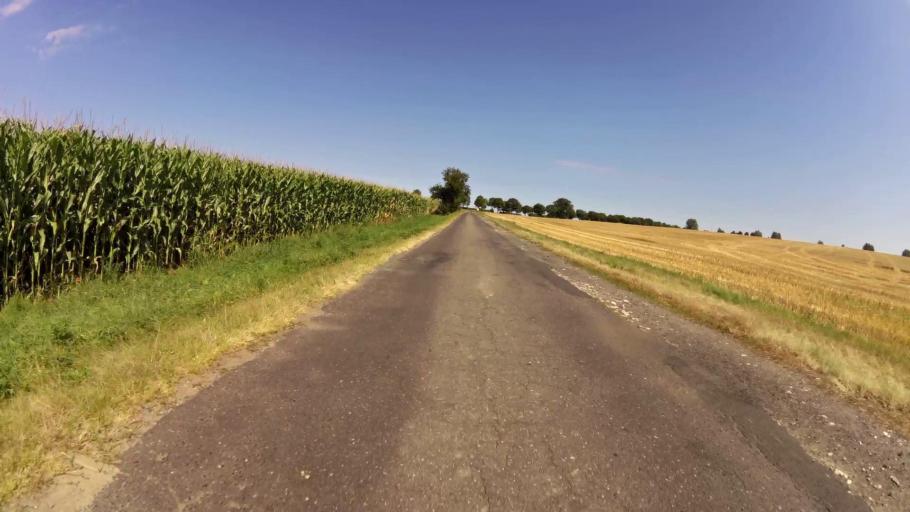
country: PL
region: West Pomeranian Voivodeship
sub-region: Powiat stargardzki
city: Dobrzany
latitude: 53.2698
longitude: 15.4450
